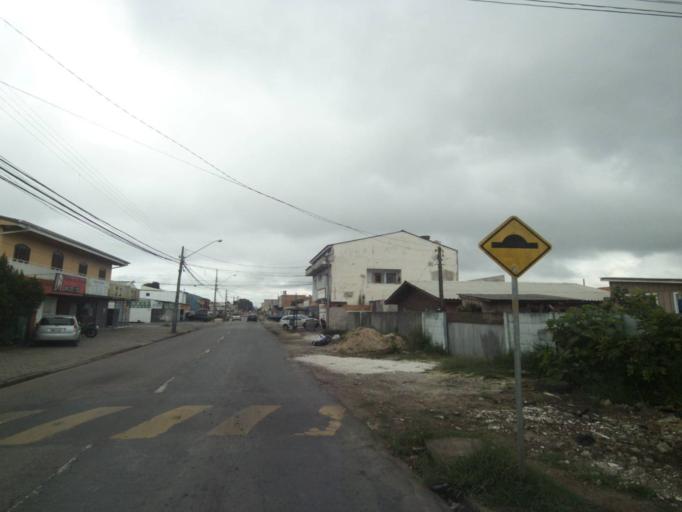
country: BR
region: Parana
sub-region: Pinhais
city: Pinhais
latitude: -25.4444
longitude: -49.1796
